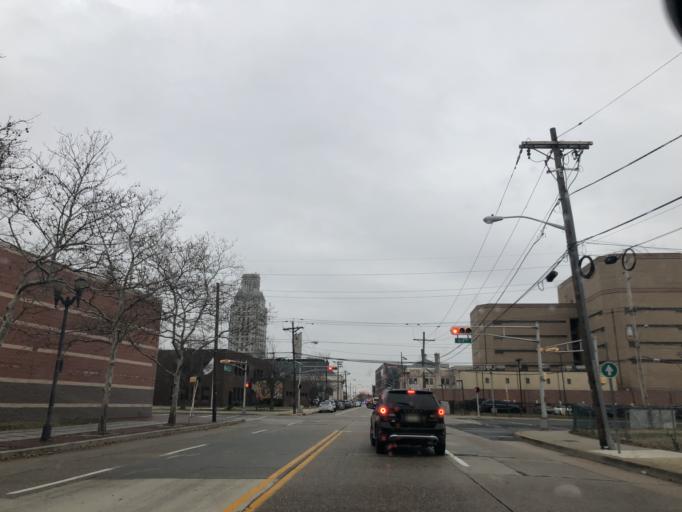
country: US
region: New Jersey
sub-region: Camden County
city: Camden
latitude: 39.9443
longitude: -75.1250
